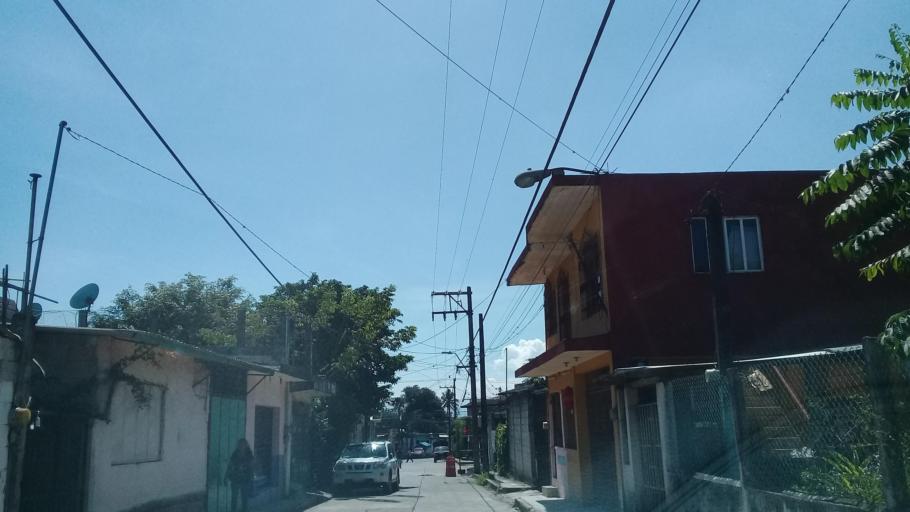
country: MX
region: Veracruz
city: Amatlan de los Reyes
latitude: 18.8484
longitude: -96.9162
